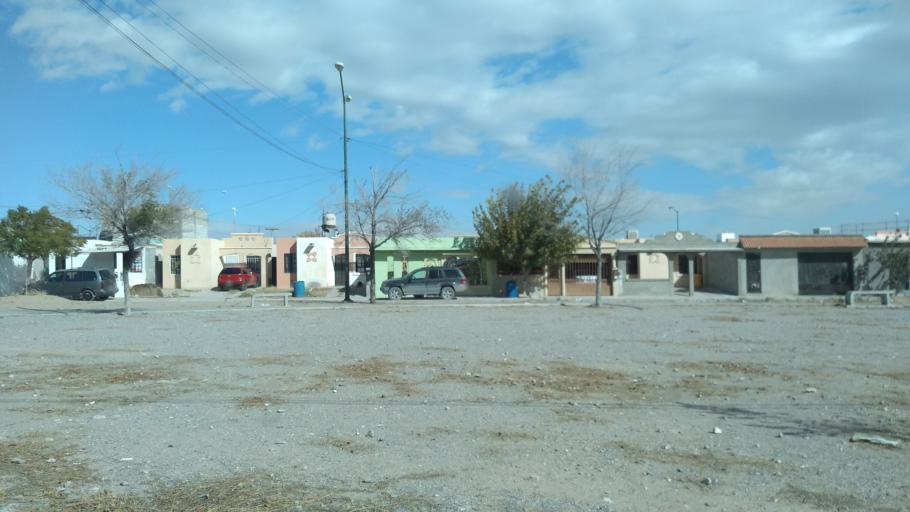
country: US
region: Texas
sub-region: El Paso County
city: Socorro Mission Number 1 Colonia
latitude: 31.5855
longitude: -106.3546
